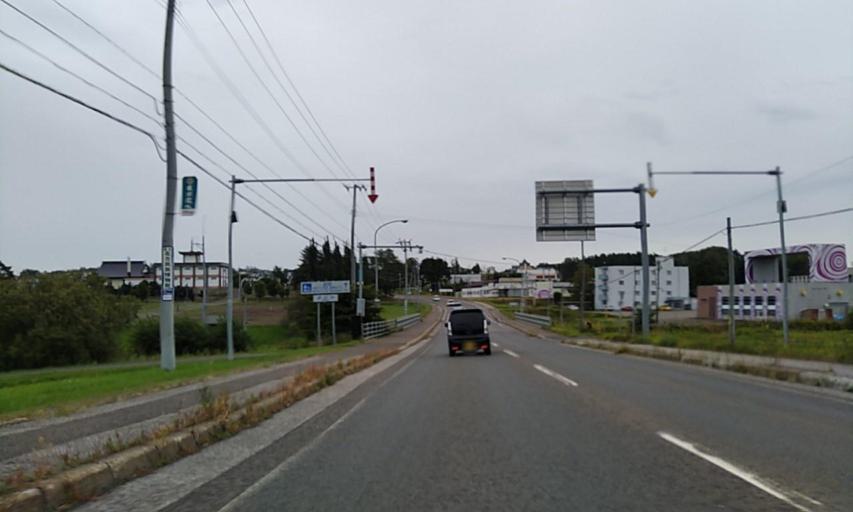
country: JP
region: Hokkaido
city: Bihoro
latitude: 43.9131
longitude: 144.1772
